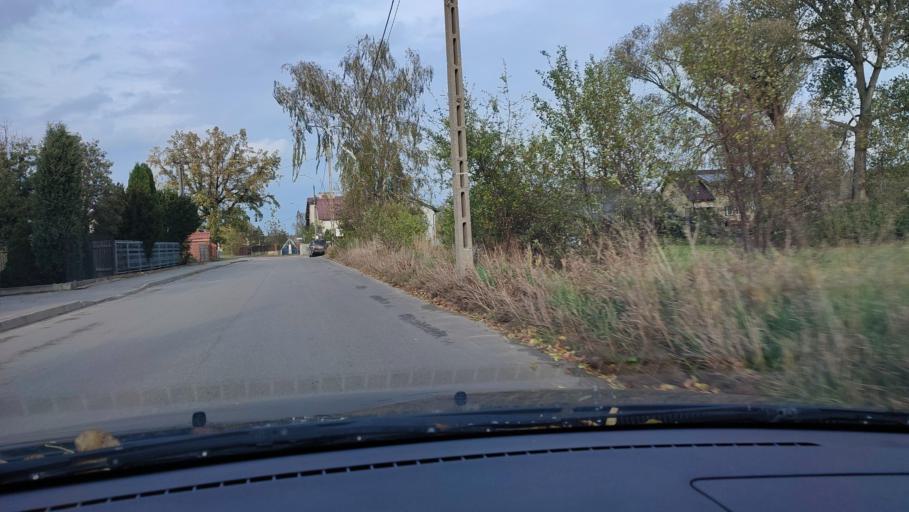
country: PL
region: Masovian Voivodeship
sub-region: Powiat mlawski
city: Mlawa
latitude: 53.1338
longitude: 20.3636
